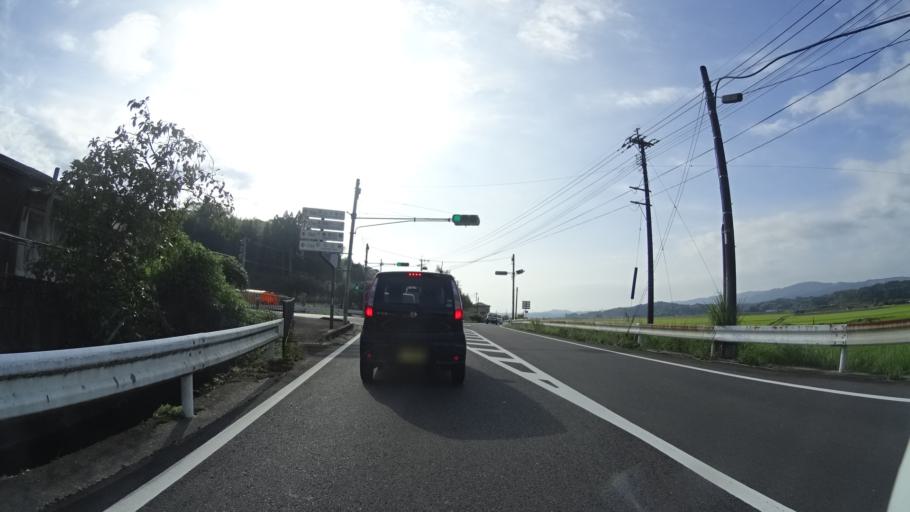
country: JP
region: Kagoshima
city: Okuchi-shinohara
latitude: 32.0224
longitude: 130.6122
